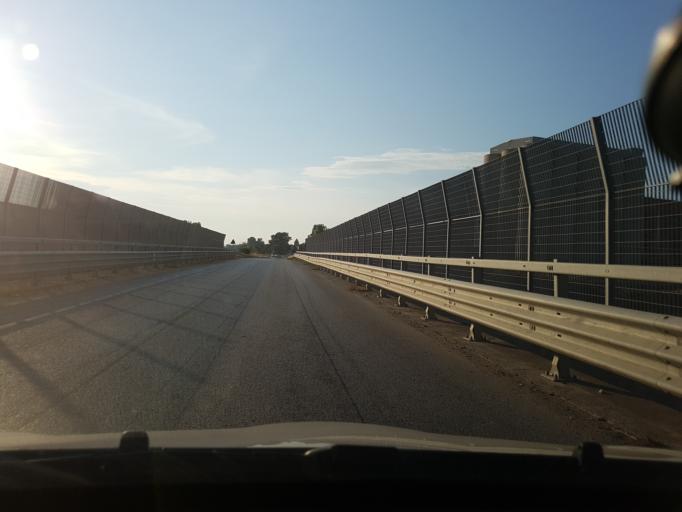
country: IT
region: Apulia
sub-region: Provincia di Foggia
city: Carapelle
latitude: 41.4009
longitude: 15.6521
